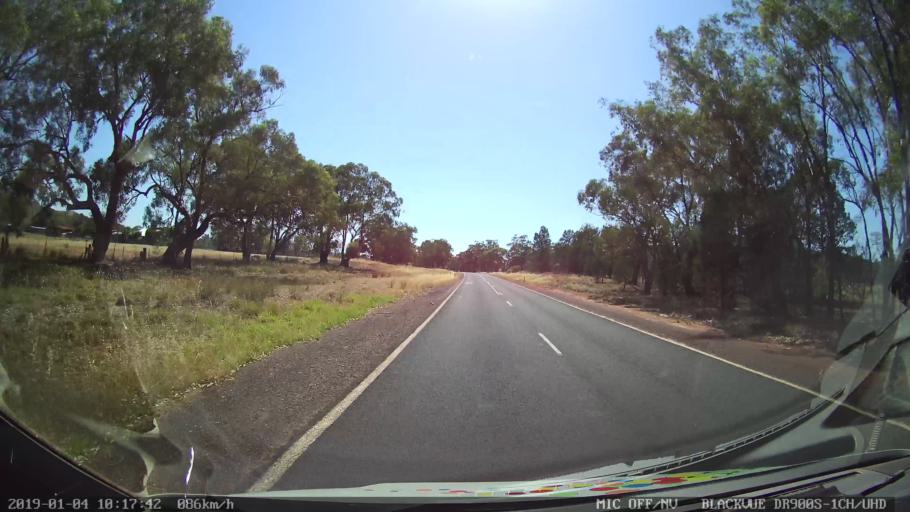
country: AU
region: New South Wales
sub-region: Cabonne
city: Canowindra
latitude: -33.3838
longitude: 148.4554
